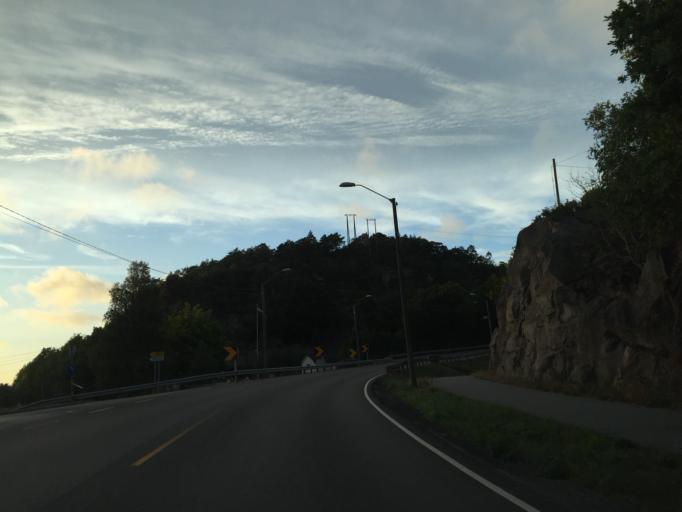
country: NO
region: Ostfold
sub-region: Fredrikstad
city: Fredrikstad
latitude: 59.1816
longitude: 10.9262
